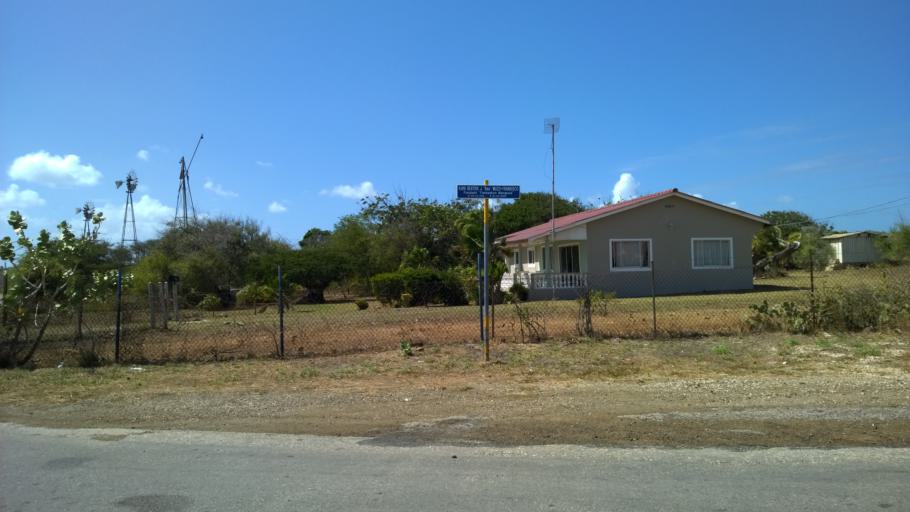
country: CW
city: Dorp Soto
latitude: 12.2598
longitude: -69.0859
